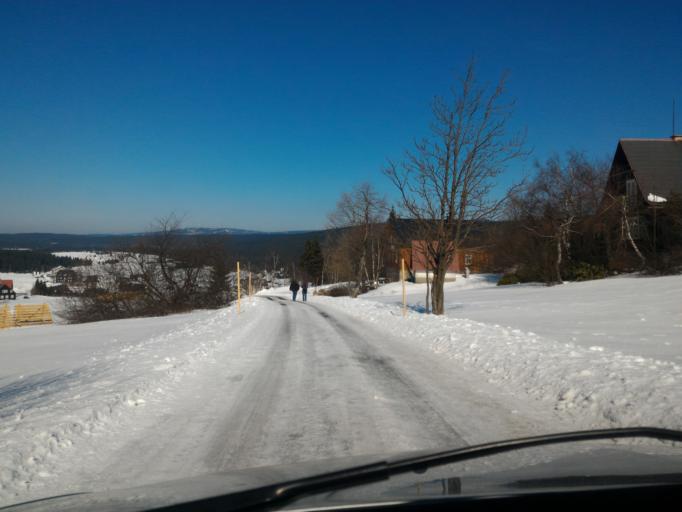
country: CZ
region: Liberecky
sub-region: Okres Jablonec nad Nisou
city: Korenov
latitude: 50.8142
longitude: 15.3525
